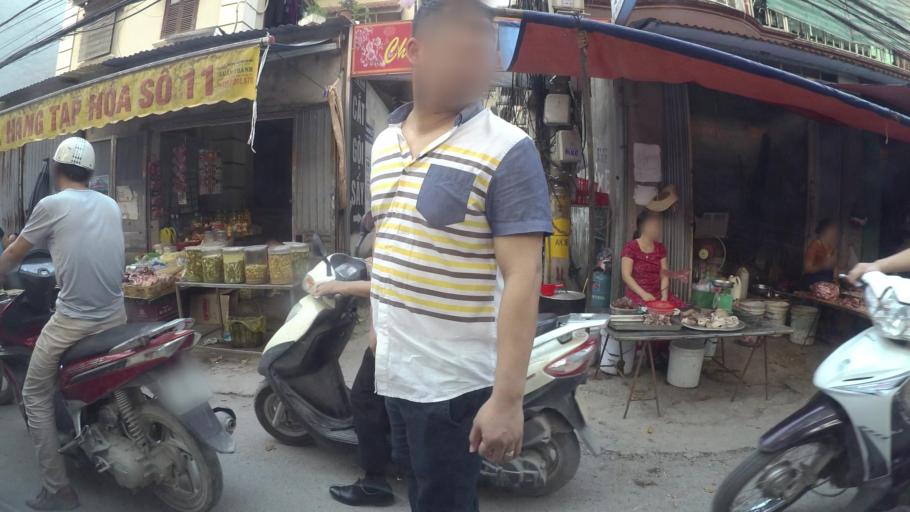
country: VN
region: Ha Noi
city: Ha Dong
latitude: 20.9934
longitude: 105.7298
